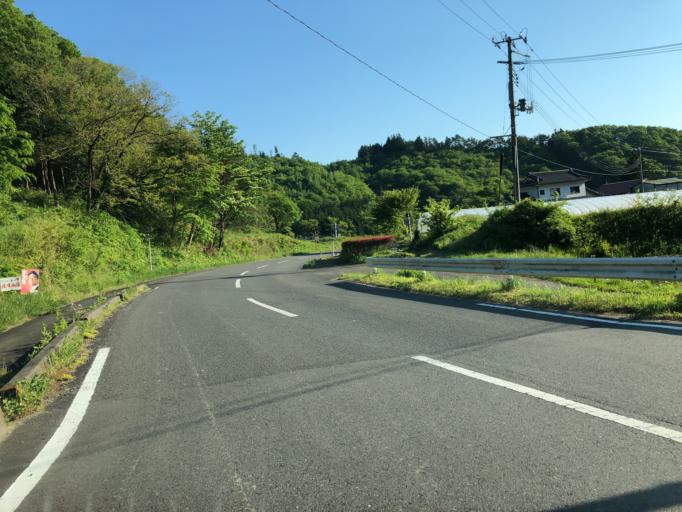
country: JP
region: Ibaraki
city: Kitaibaraki
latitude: 36.9212
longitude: 140.5433
